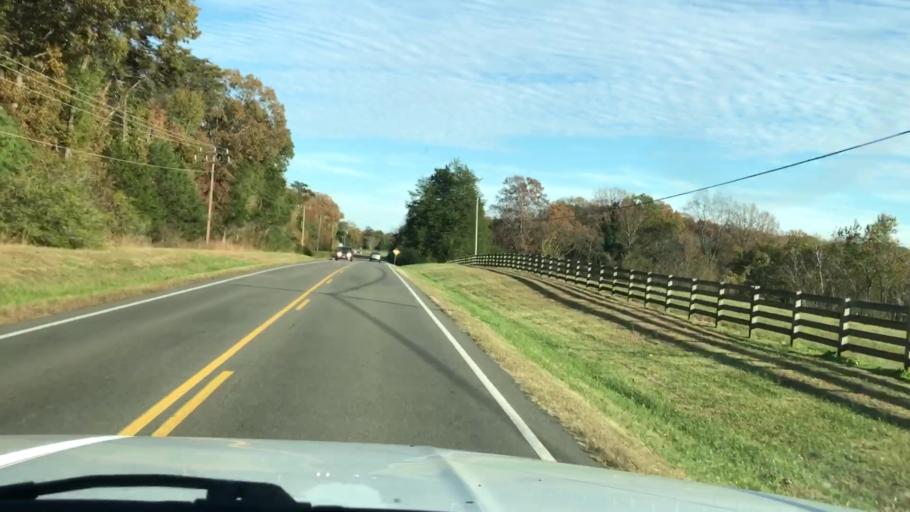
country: US
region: Virginia
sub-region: Goochland County
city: Goochland
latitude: 37.6372
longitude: -77.8095
